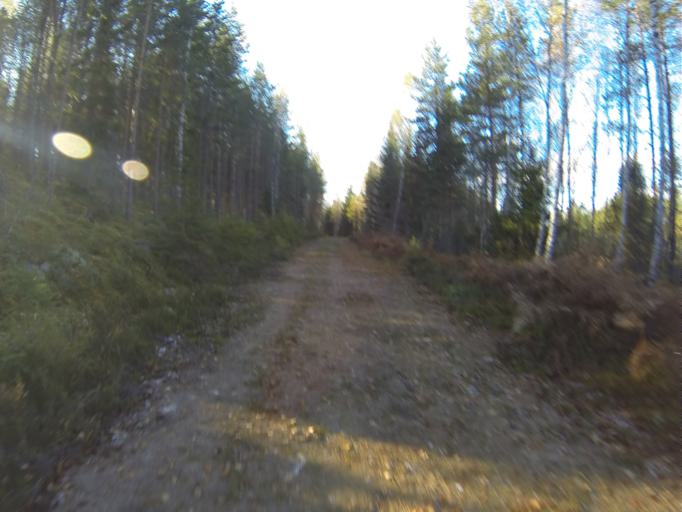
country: FI
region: Varsinais-Suomi
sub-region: Salo
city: Saerkisalo
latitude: 60.2245
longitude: 22.9531
